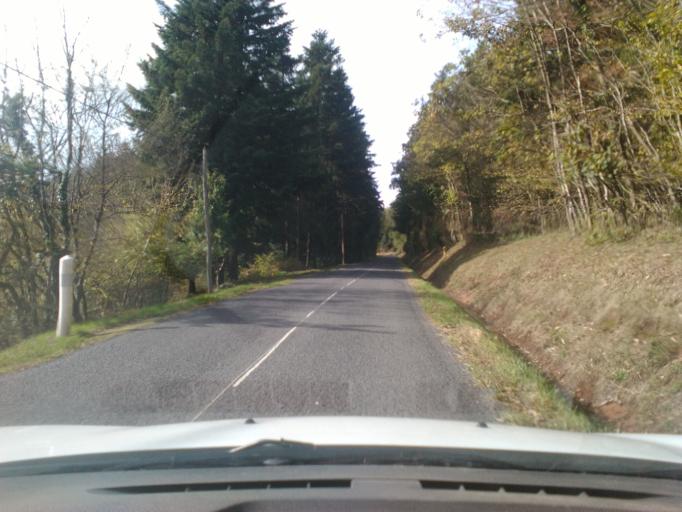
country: FR
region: Lorraine
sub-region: Departement des Vosges
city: Sainte-Marguerite
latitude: 48.2956
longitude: 6.9978
